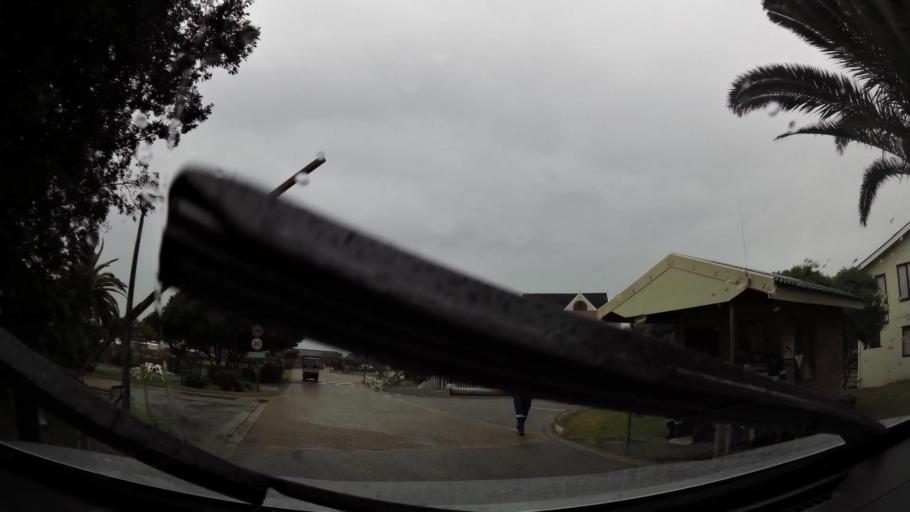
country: ZA
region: Western Cape
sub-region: Eden District Municipality
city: Mossel Bay
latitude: -34.0505
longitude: 22.2737
